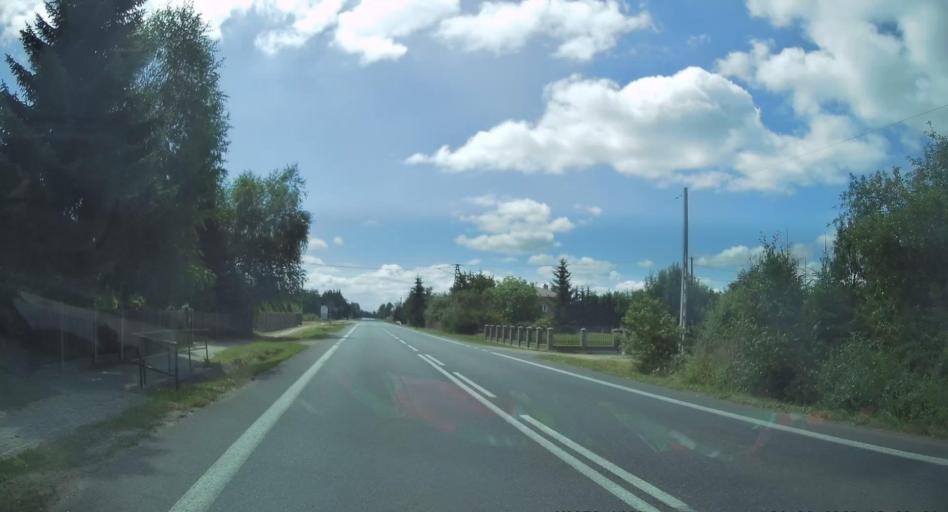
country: PL
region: Subcarpathian Voivodeship
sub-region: Powiat mielecki
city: Przeclaw
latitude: 50.1659
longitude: 21.4881
